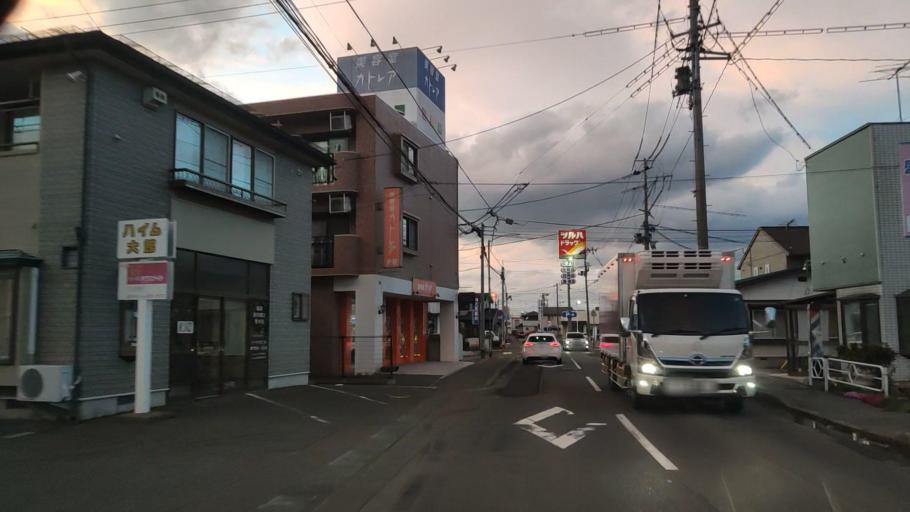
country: JP
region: Iwate
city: Morioka-shi
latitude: 39.7127
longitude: 141.1100
